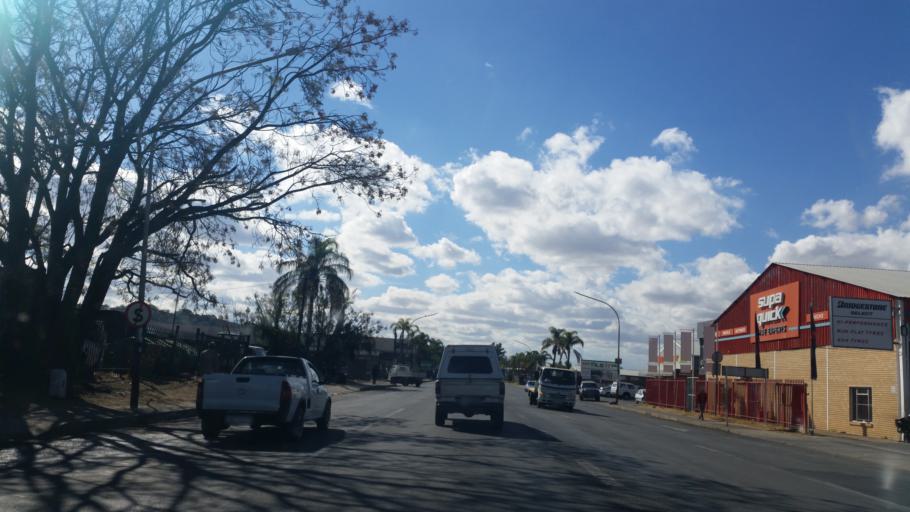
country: ZA
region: KwaZulu-Natal
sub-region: uThukela District Municipality
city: Ladysmith
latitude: -28.5651
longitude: 29.7795
